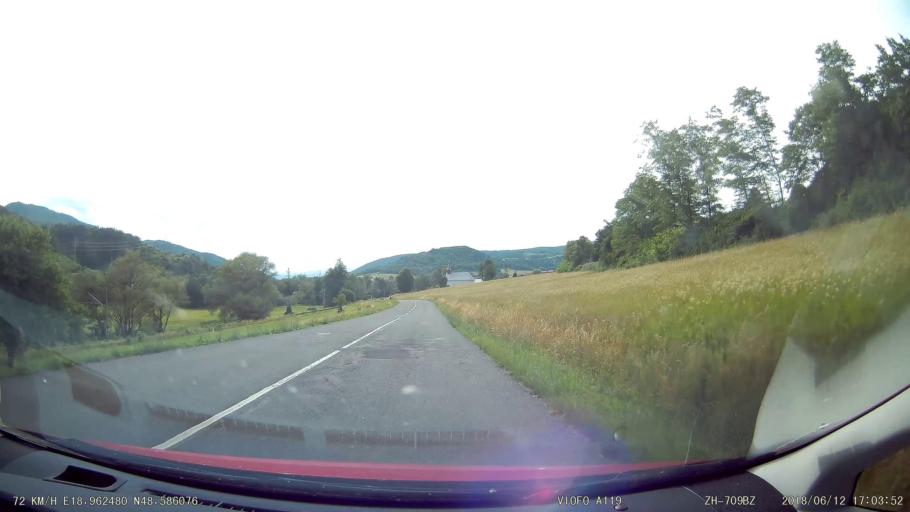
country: SK
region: Banskobystricky
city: Ziar nad Hronom
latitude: 48.5865
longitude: 18.9629
